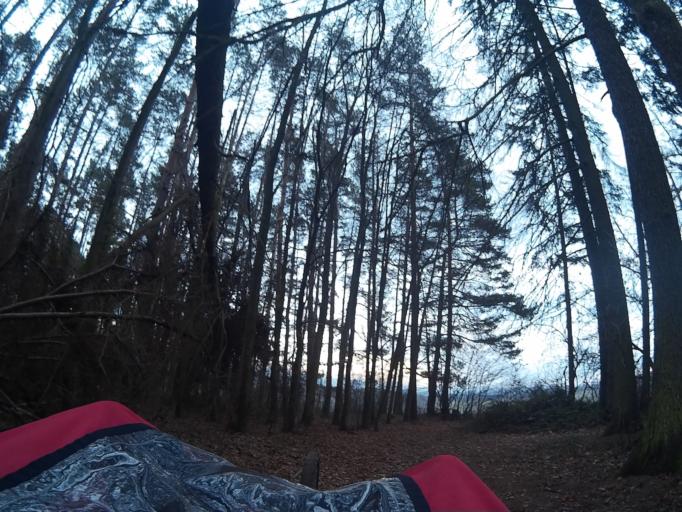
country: CZ
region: Plzensky
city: Stary Plzenec
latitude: 49.6804
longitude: 13.4813
